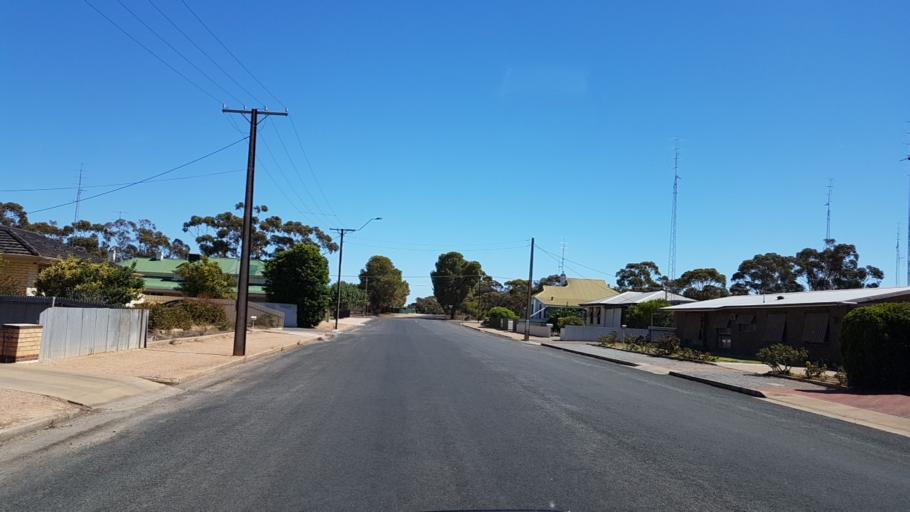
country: AU
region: South Australia
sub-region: Copper Coast
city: Kadina
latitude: -33.9595
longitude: 137.7136
